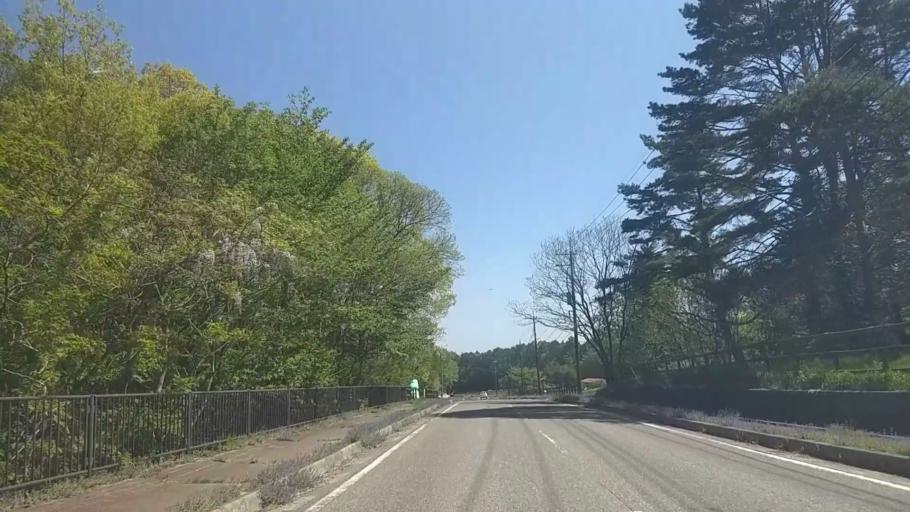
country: JP
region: Yamanashi
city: Nirasaki
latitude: 35.9100
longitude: 138.4322
